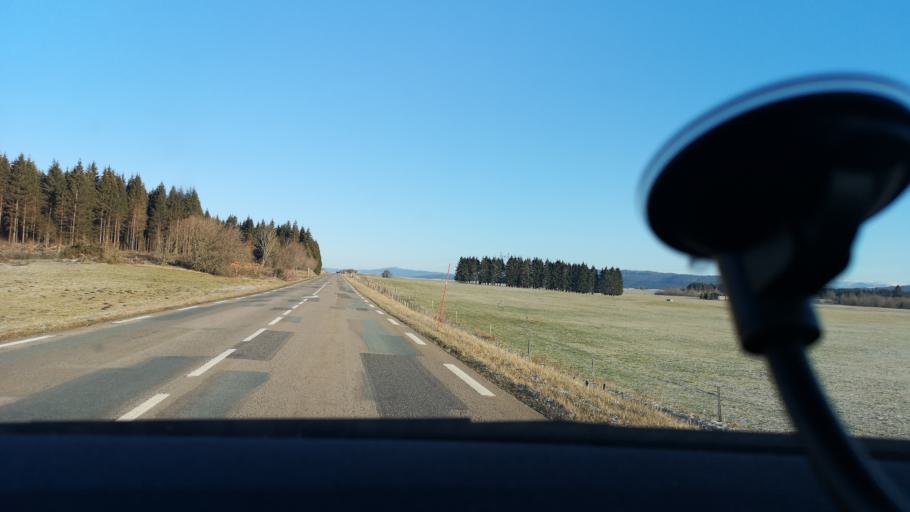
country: FR
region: Franche-Comte
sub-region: Departement du Doubs
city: Frasne
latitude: 46.8374
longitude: 6.1177
